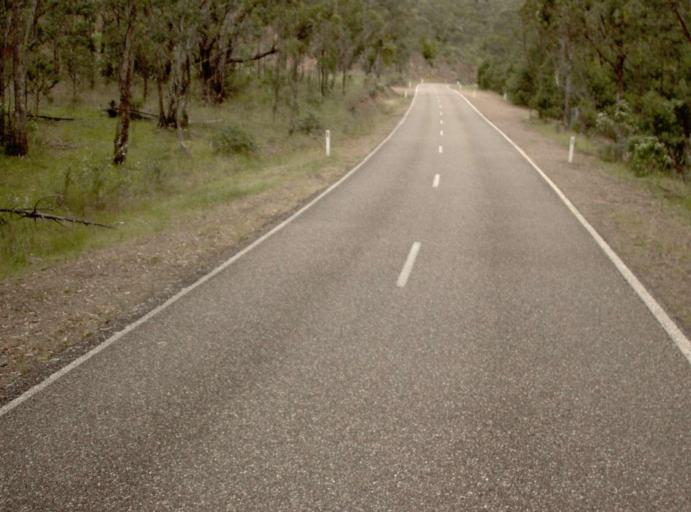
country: AU
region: Victoria
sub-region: East Gippsland
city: Bairnsdale
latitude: -37.5388
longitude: 147.2082
